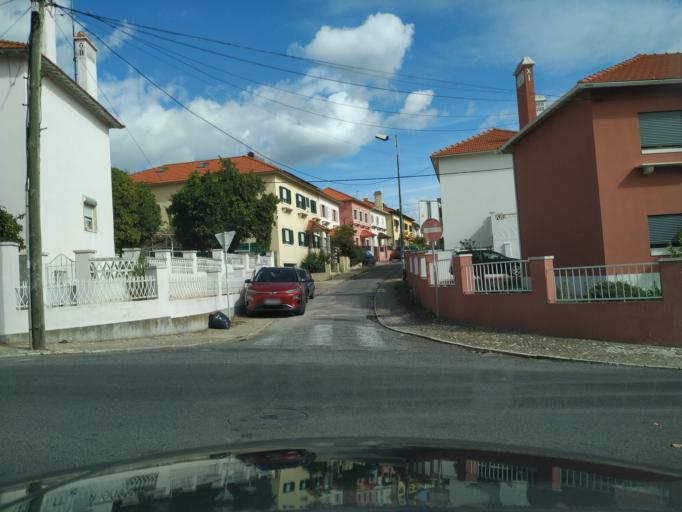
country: PT
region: Lisbon
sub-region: Loures
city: Moscavide
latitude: 38.7704
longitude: -9.1170
